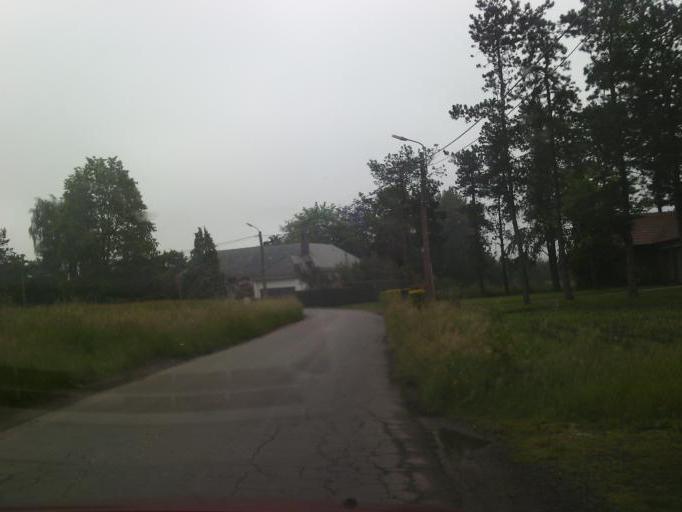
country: BE
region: Flanders
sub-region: Provincie Oost-Vlaanderen
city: Berlare
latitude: 50.9983
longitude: 4.0468
